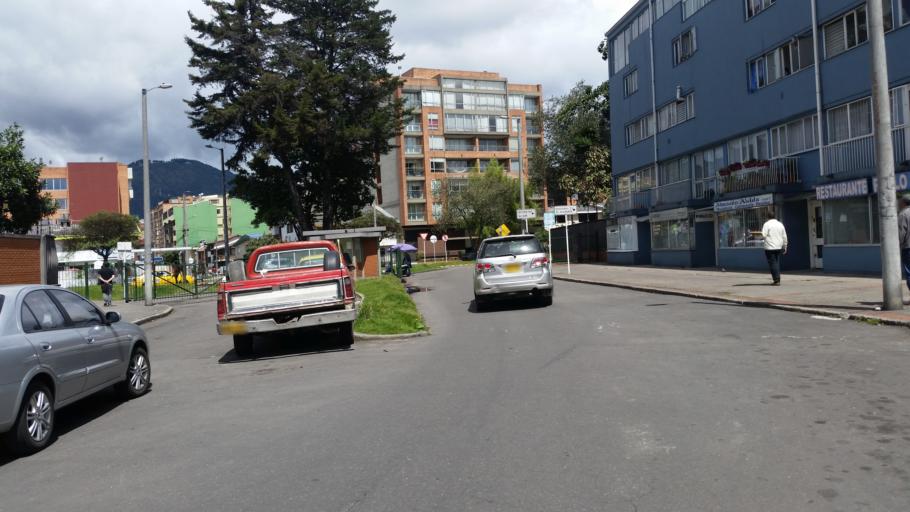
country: CO
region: Bogota D.C.
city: Bogota
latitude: 4.6492
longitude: -74.0860
